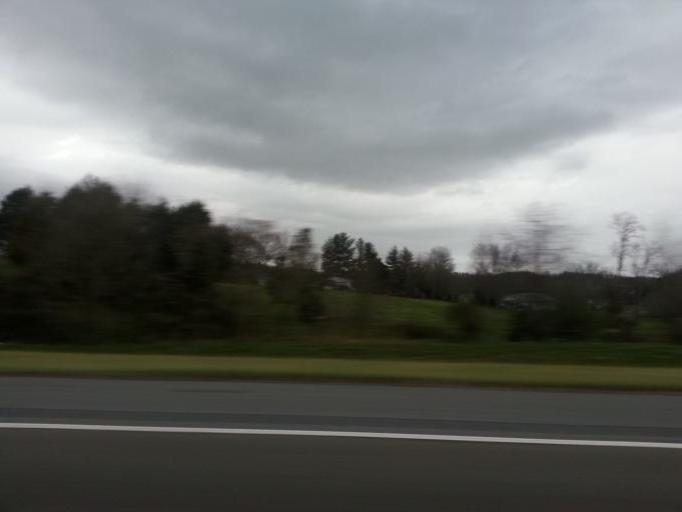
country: US
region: Tennessee
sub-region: Carter County
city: Pine Crest
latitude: 36.3153
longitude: -82.3063
